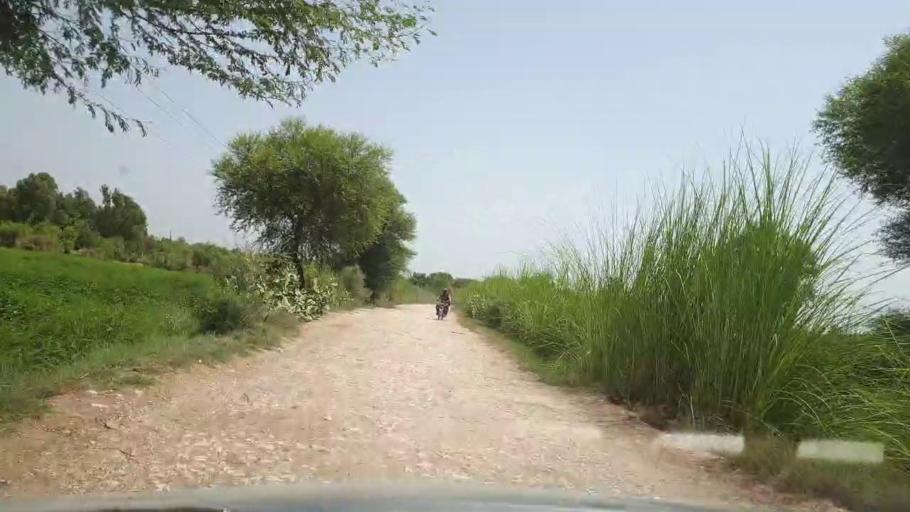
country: PK
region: Sindh
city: Pano Aqil
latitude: 27.8182
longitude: 69.2300
